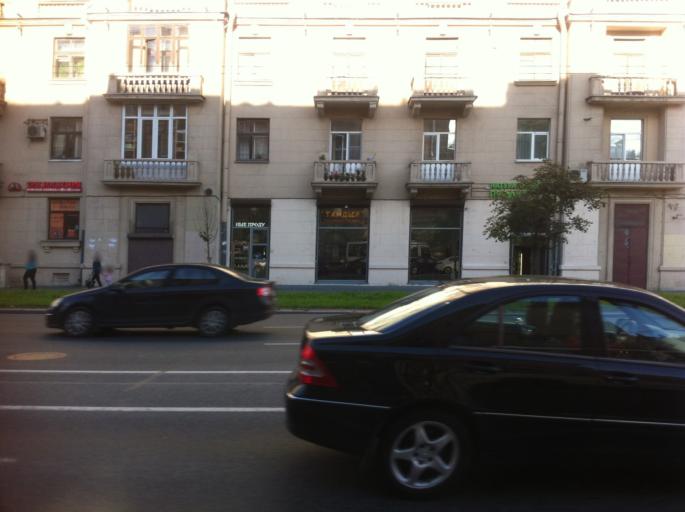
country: RU
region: St.-Petersburg
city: Avtovo
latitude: 59.8706
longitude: 30.2596
